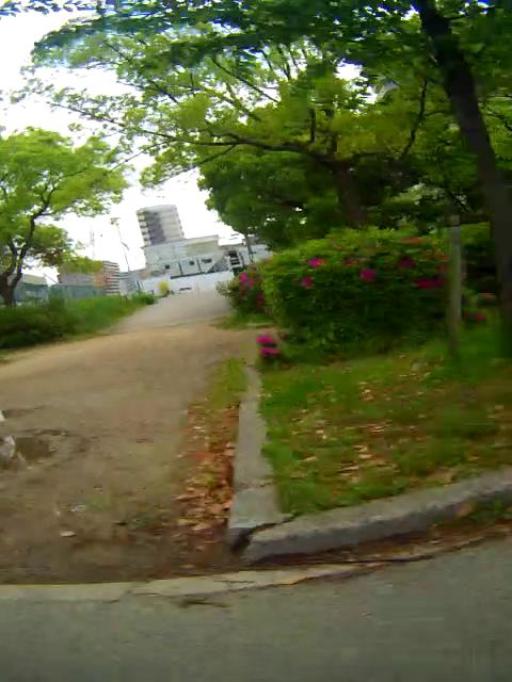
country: JP
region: Osaka
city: Osaka-shi
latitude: 34.6932
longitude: 135.5225
